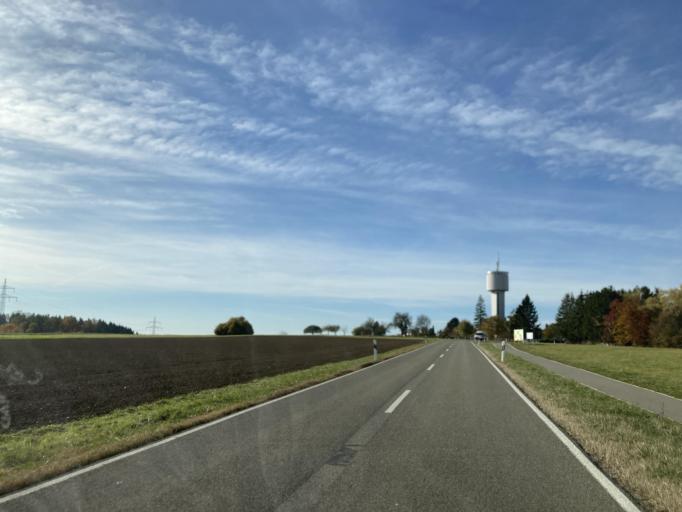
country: DE
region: Baden-Wuerttemberg
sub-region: Tuebingen Region
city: Bodelshausen
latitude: 48.3791
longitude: 8.9767
